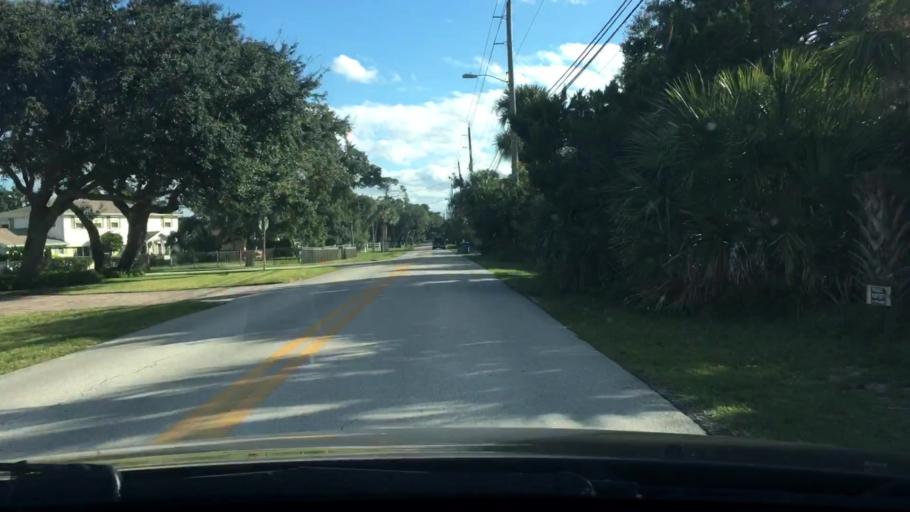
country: US
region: Florida
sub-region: Volusia County
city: Ormond-by-the-Sea
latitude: 29.3488
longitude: -81.0737
